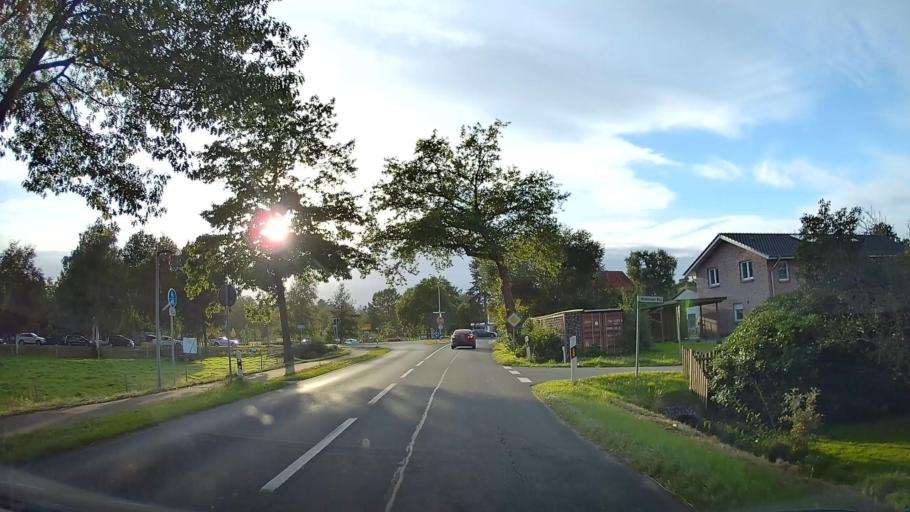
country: DE
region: Lower Saxony
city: Ottersberg
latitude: 53.0712
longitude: 9.1680
